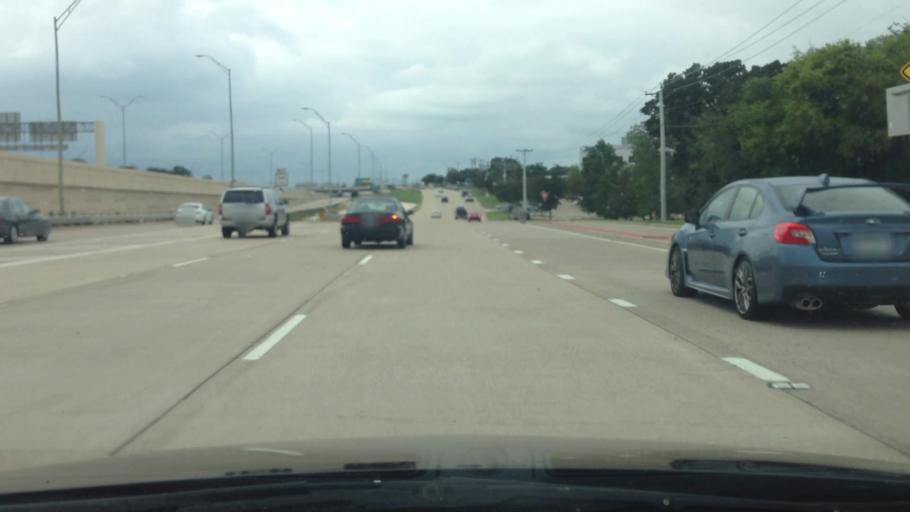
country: US
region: Texas
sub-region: Tarrant County
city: Grapevine
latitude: 32.9347
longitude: -97.0965
